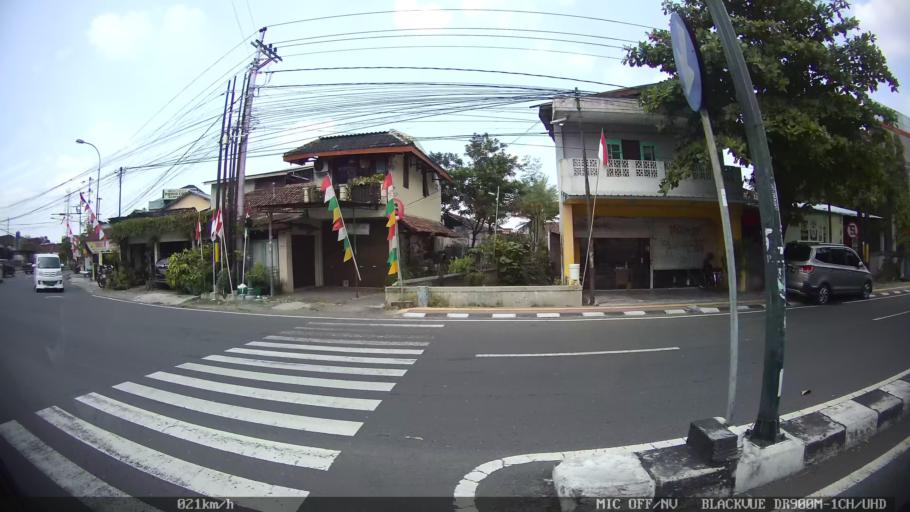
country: ID
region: Daerah Istimewa Yogyakarta
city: Yogyakarta
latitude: -7.8175
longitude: 110.3862
